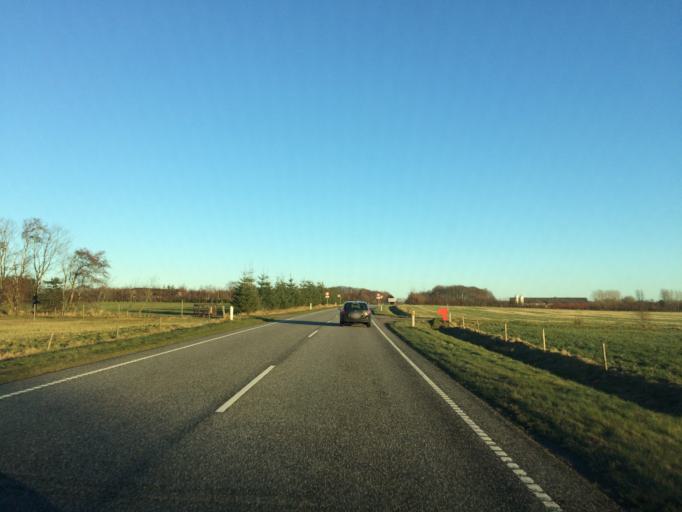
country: DK
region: Central Jutland
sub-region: Herning Kommune
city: Vildbjerg
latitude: 56.1890
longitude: 8.7850
